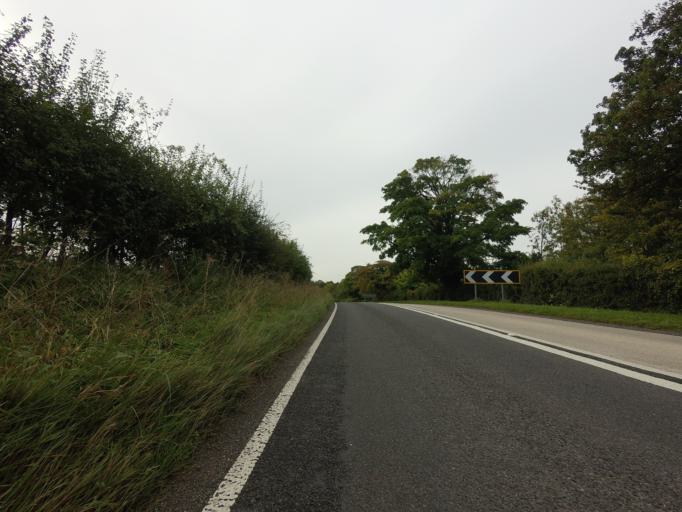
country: GB
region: England
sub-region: Hertfordshire
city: Reed
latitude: 52.0188
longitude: 0.0298
